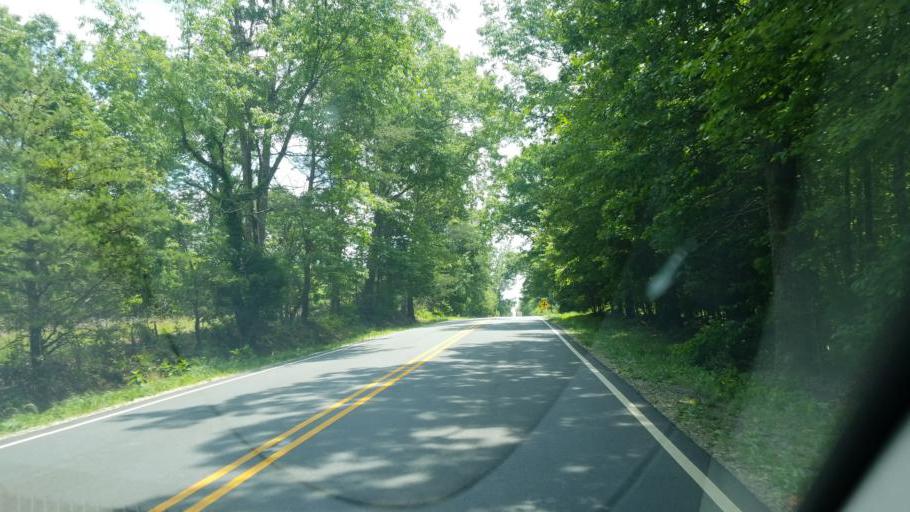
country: US
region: Virginia
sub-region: Nelson County
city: Lovingston
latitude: 37.5733
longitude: -78.8591
